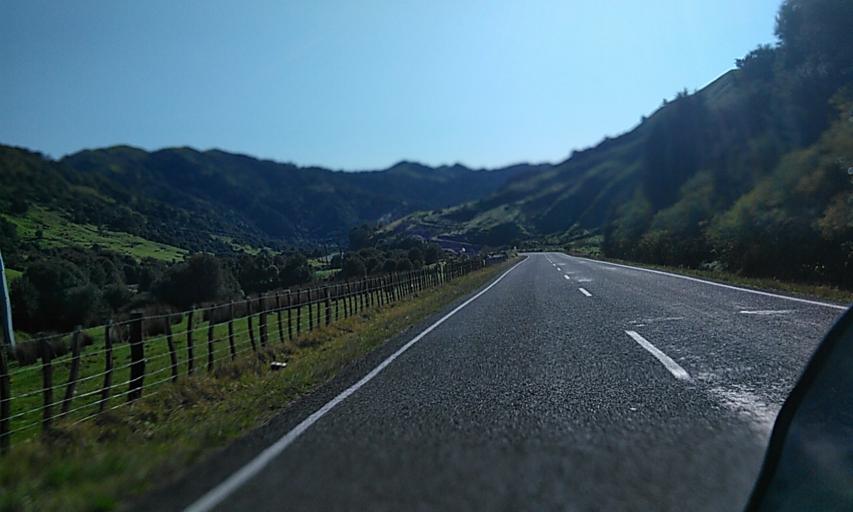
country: NZ
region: Gisborne
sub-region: Gisborne District
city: Gisborne
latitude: -38.5906
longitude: 177.9888
